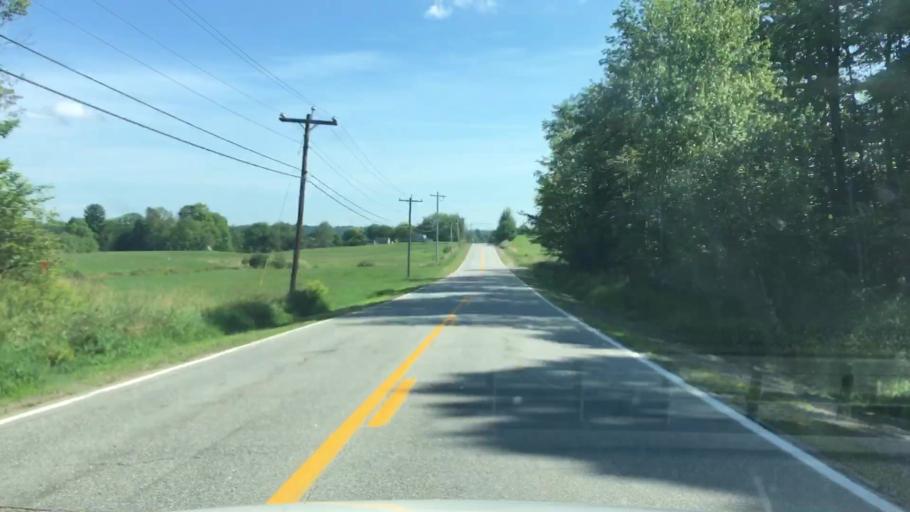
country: US
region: Maine
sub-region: Androscoggin County
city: Greene
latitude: 44.2175
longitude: -70.0898
